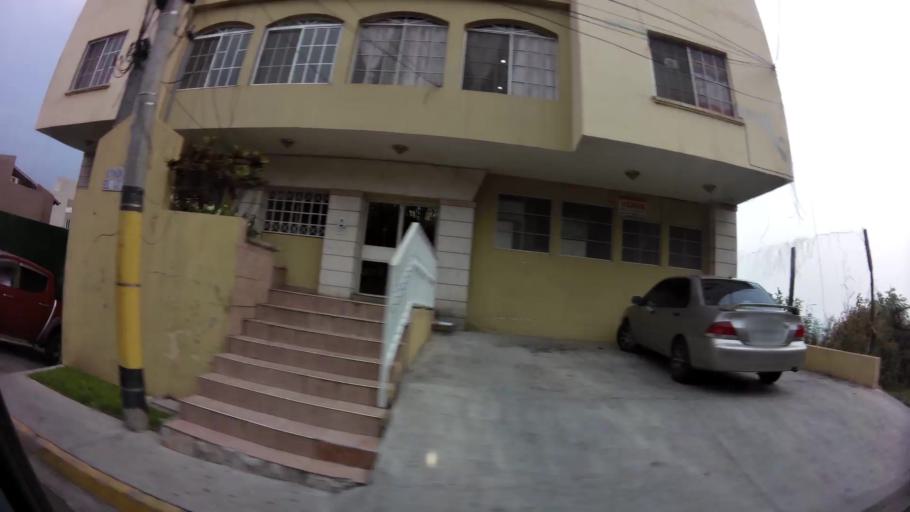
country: HN
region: Francisco Morazan
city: Tegucigalpa
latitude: 14.0931
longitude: -87.1801
